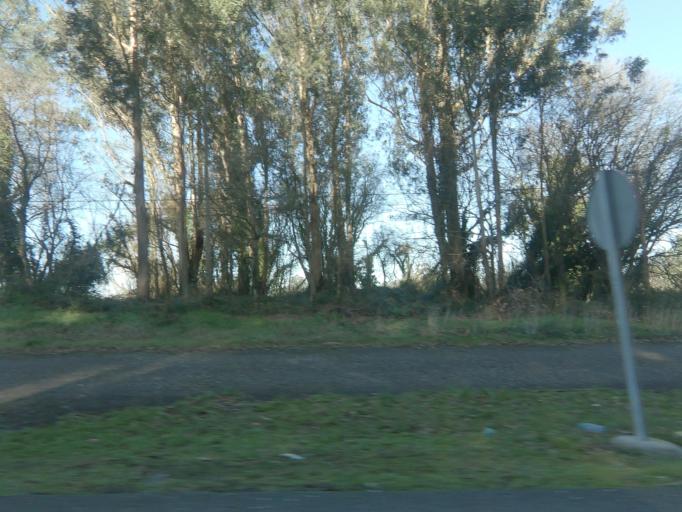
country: ES
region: Galicia
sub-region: Provincia da Coruna
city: Vedra
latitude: 42.8120
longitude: -8.4795
